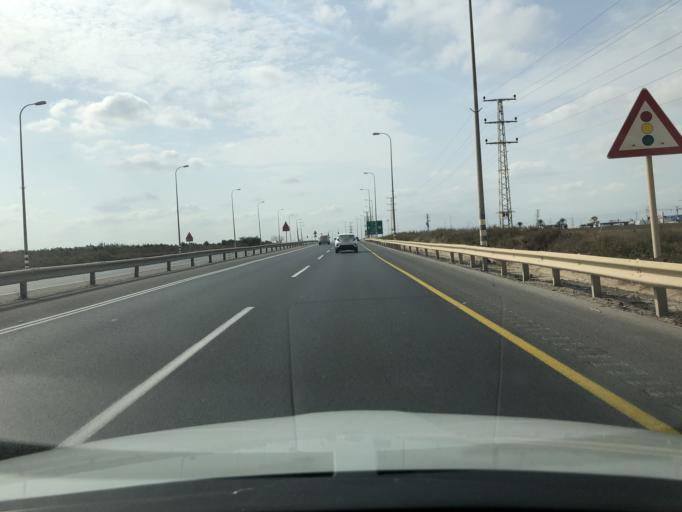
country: IL
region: Central District
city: Tirah
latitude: 32.2350
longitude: 34.9860
